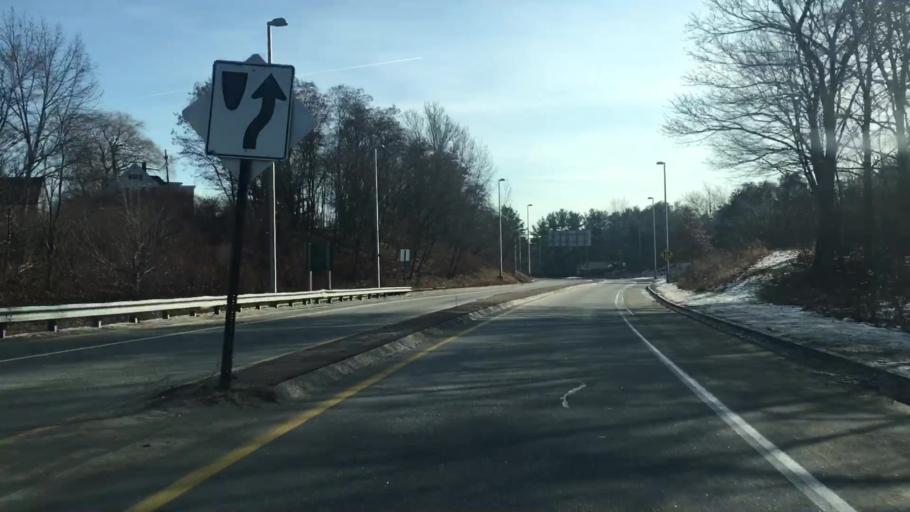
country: US
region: Maine
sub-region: Androscoggin County
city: Lewiston
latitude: 44.1114
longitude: -70.2072
